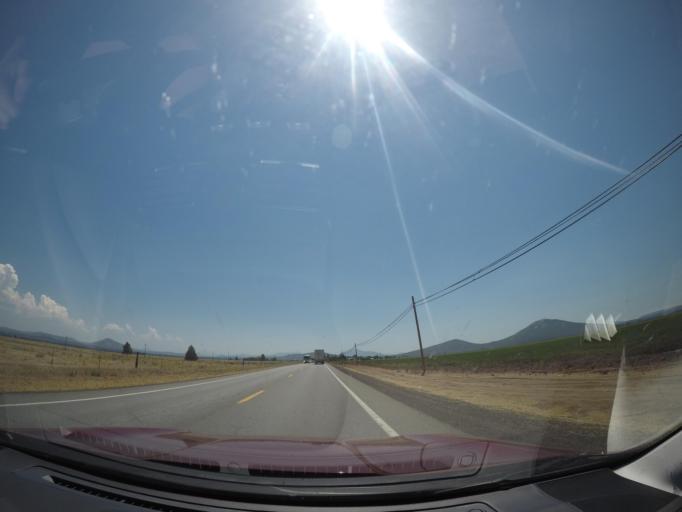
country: US
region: California
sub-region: Shasta County
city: Burney
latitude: 41.0433
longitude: -121.4099
